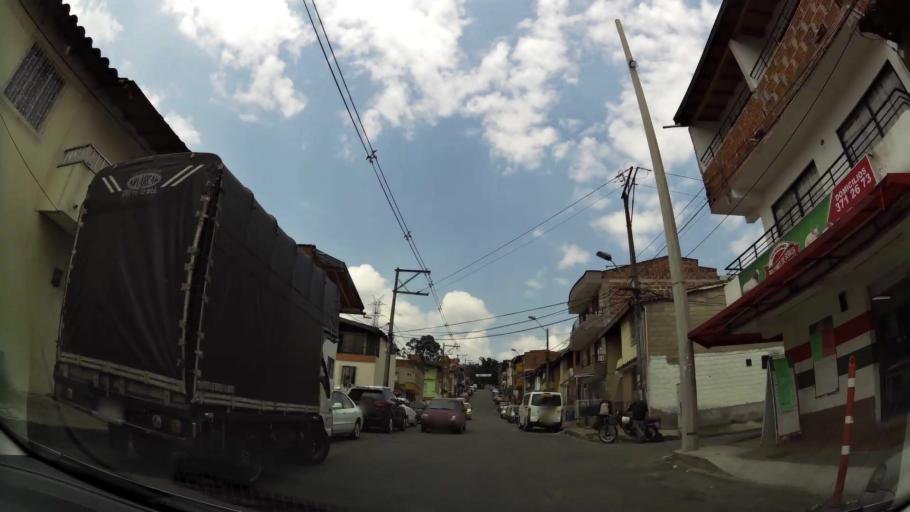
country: CO
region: Antioquia
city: Itagui
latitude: 6.1827
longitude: -75.6024
